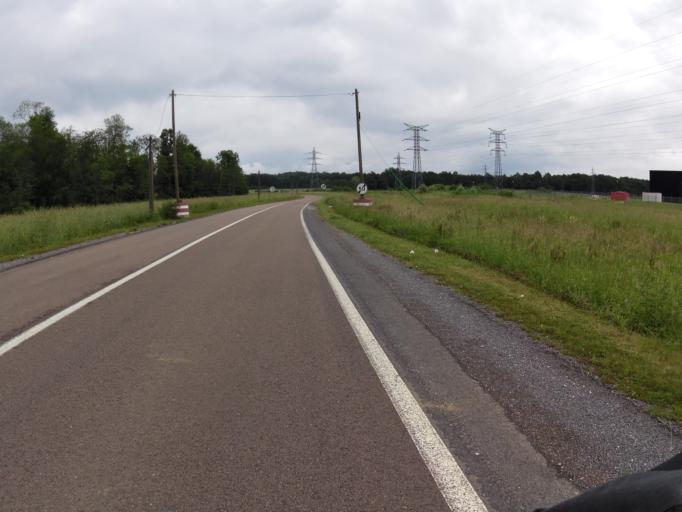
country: FR
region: Champagne-Ardenne
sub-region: Departement de la Haute-Marne
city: Saint-Dizier
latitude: 48.6564
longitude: 4.9395
